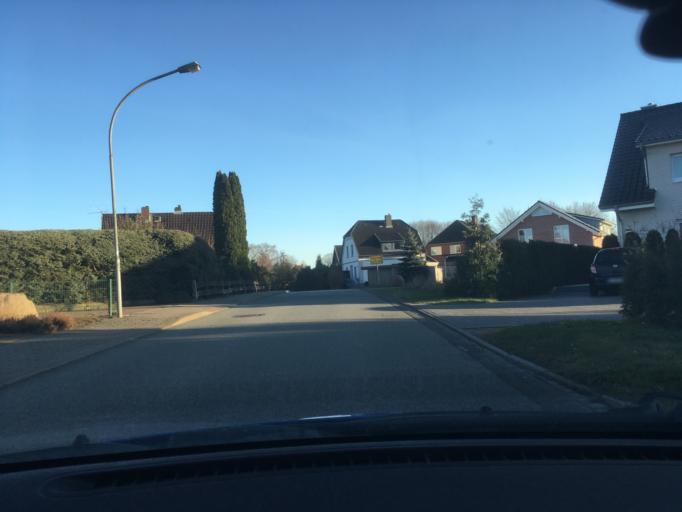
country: DE
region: Lower Saxony
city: Seevetal
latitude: 53.4086
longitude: 9.9622
